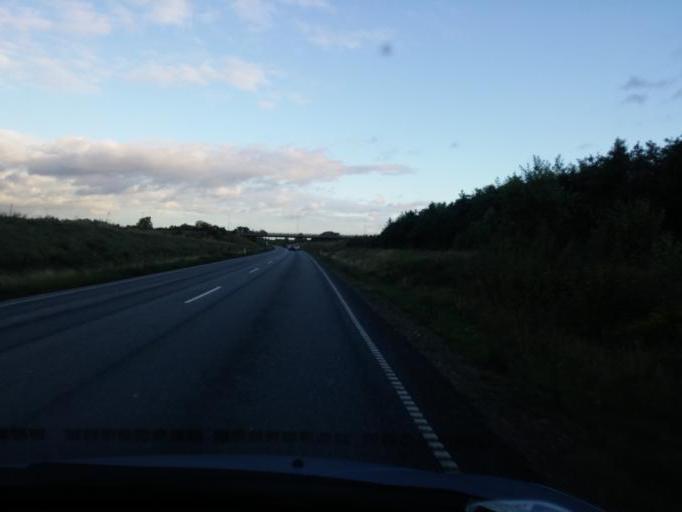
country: DK
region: South Denmark
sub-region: Odense Kommune
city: Bullerup
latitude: 55.4155
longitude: 10.4697
